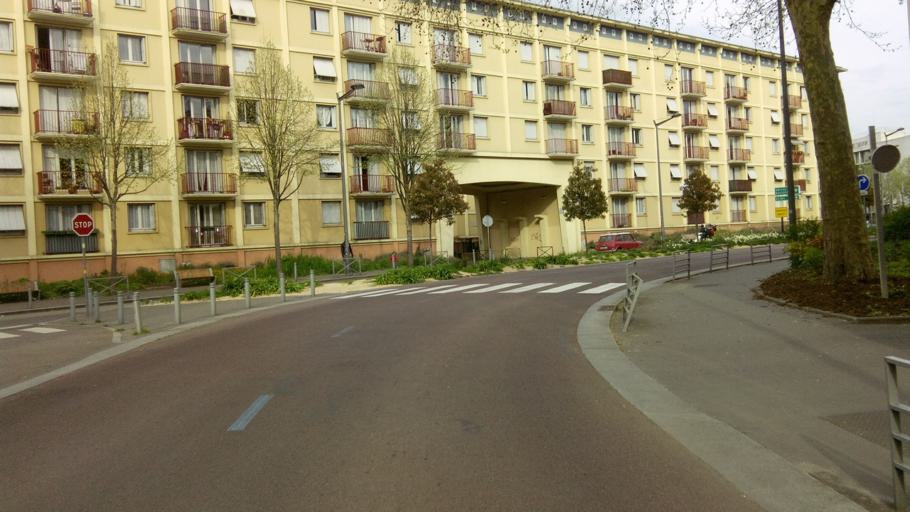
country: FR
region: Haute-Normandie
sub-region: Departement de la Seine-Maritime
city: Rouen
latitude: 49.4382
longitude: 1.1038
